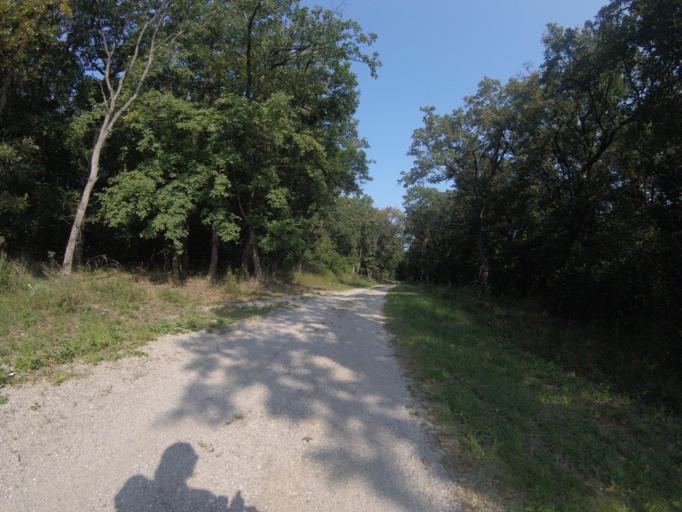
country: HU
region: Gyor-Moson-Sopron
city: Fertorakos
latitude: 47.6993
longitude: 16.6566
